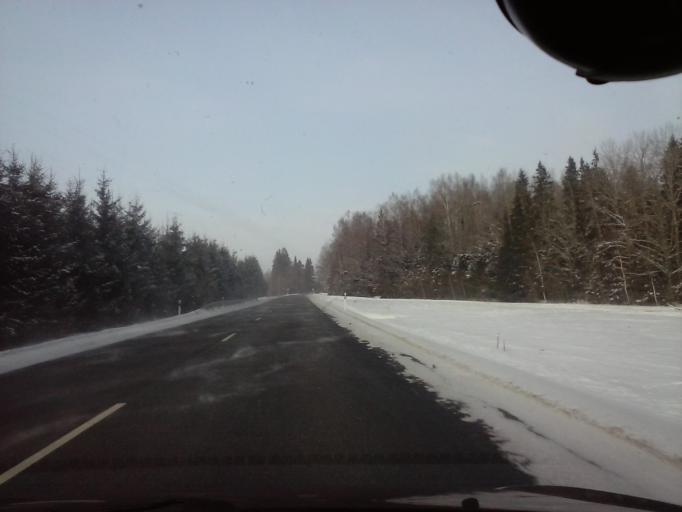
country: EE
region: Viljandimaa
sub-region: Abja vald
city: Abja-Paluoja
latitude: 58.3046
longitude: 25.2993
